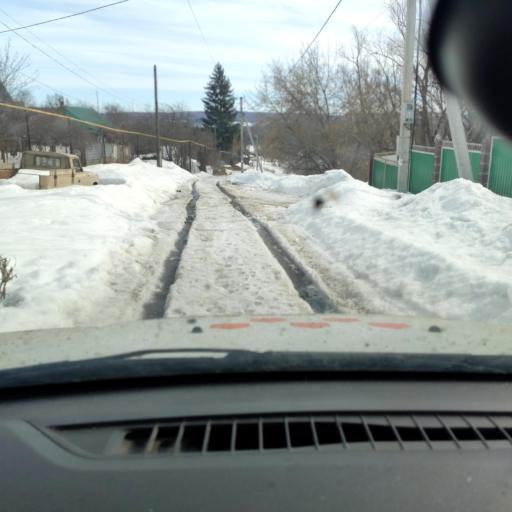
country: RU
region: Bashkortostan
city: Avdon
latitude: 54.6203
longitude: 55.6486
